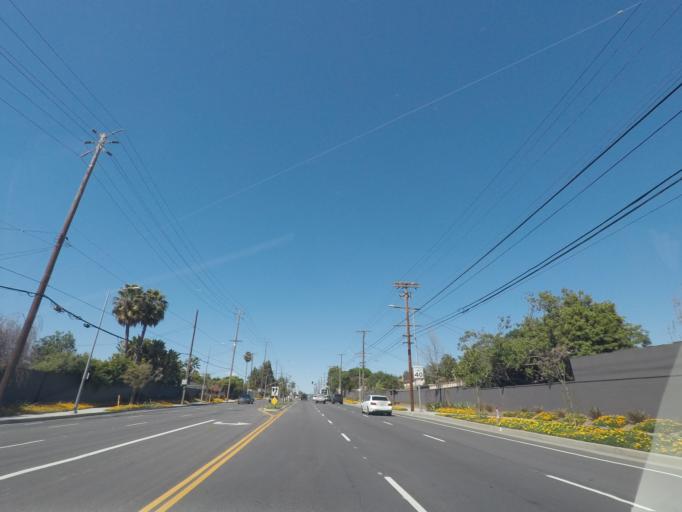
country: US
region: California
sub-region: Los Angeles County
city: Ladera Heights
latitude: 33.9620
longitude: -118.3962
